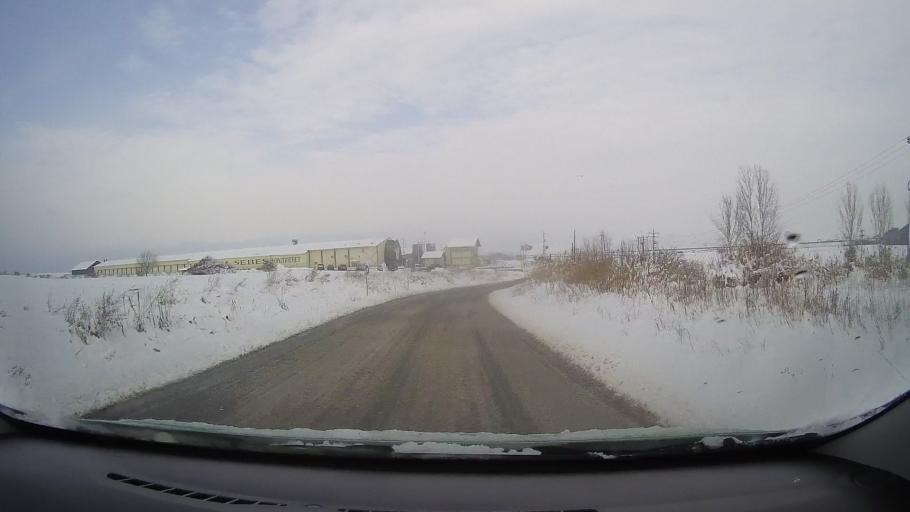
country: RO
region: Alba
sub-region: Comuna Pianu
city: Pianu de Jos
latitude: 45.9586
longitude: 23.4767
